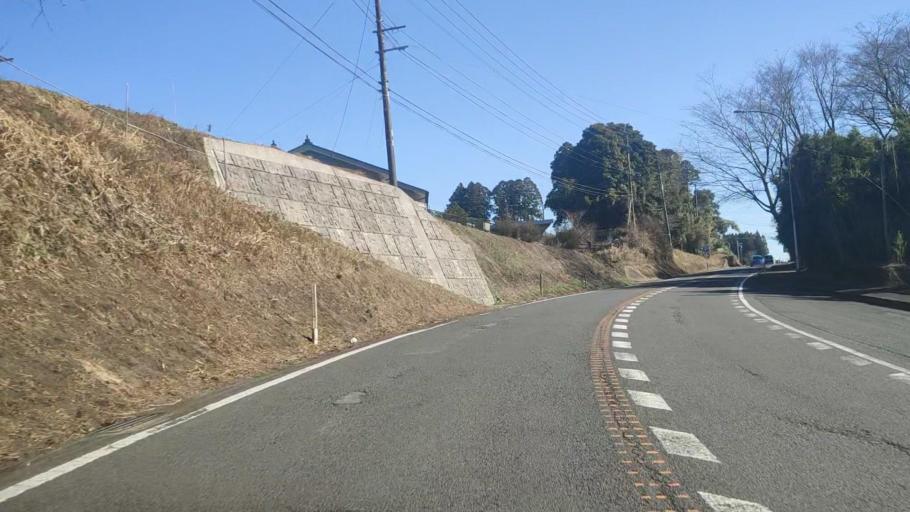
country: JP
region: Kagoshima
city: Sueyoshicho-ninokata
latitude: 31.6954
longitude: 130.9770
